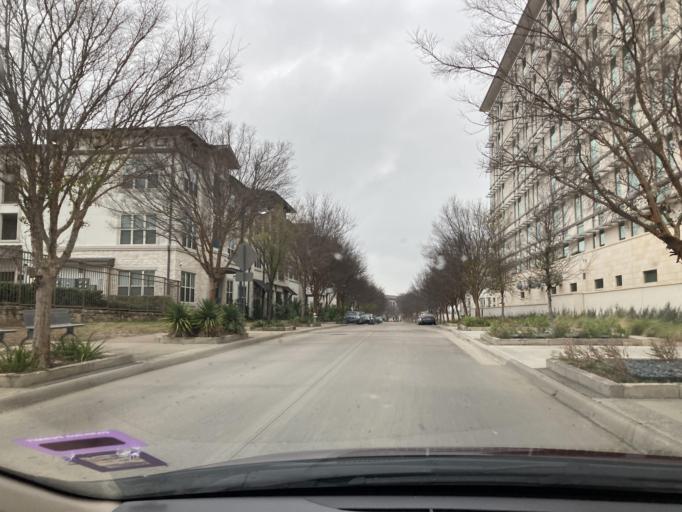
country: US
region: Texas
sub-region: Dallas County
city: University Park
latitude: 32.8924
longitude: -96.7664
